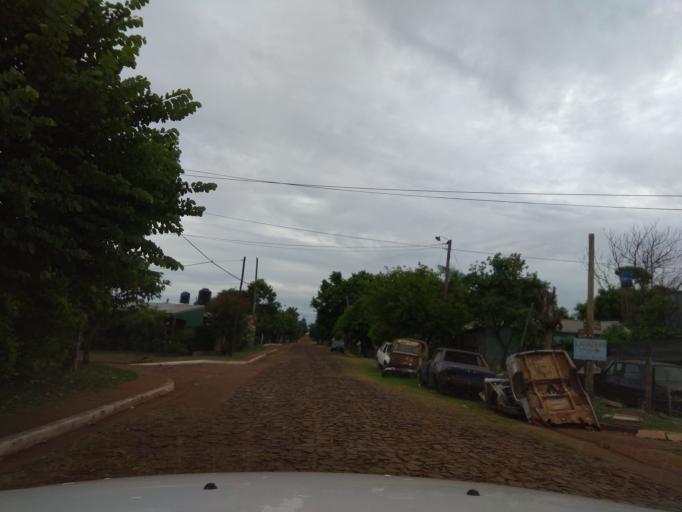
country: AR
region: Misiones
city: Garupa
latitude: -27.4453
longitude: -55.8527
